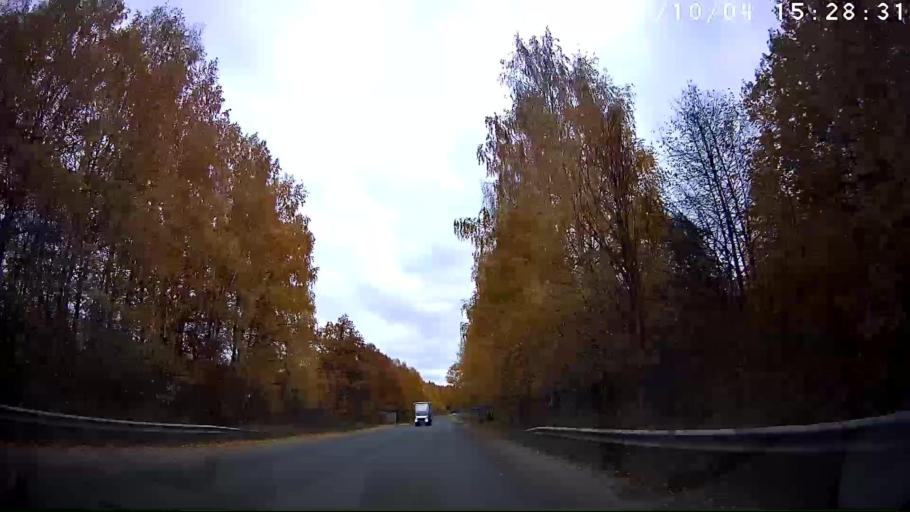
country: RU
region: Mariy-El
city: Yoshkar-Ola
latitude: 56.6091
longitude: 47.9661
